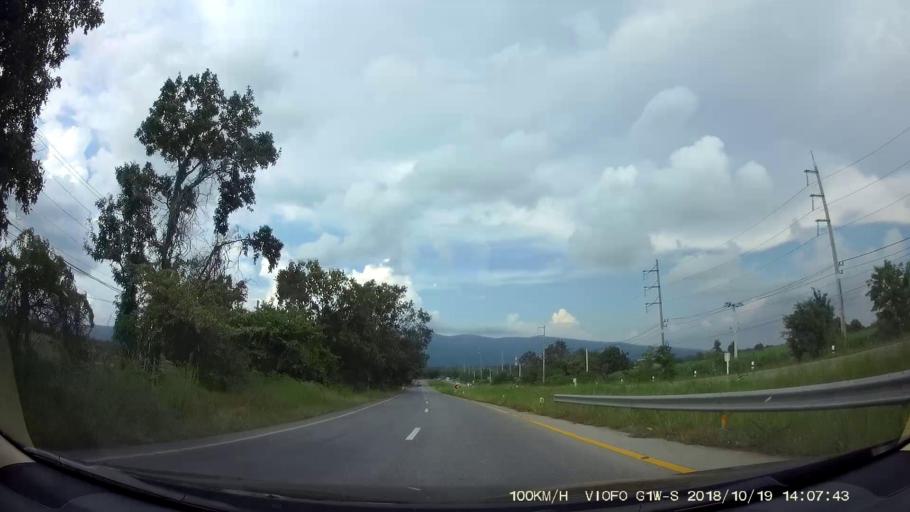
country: TH
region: Chaiyaphum
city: Chaiyaphum
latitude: 15.8975
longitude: 102.1190
